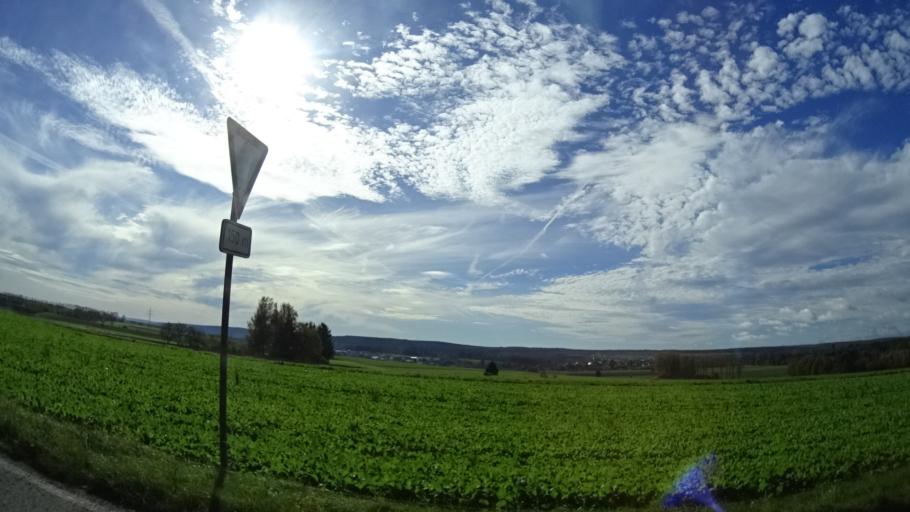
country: DE
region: Baden-Wuerttemberg
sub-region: Karlsruhe Region
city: Tiefenbronn
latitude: 48.8395
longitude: 8.8134
